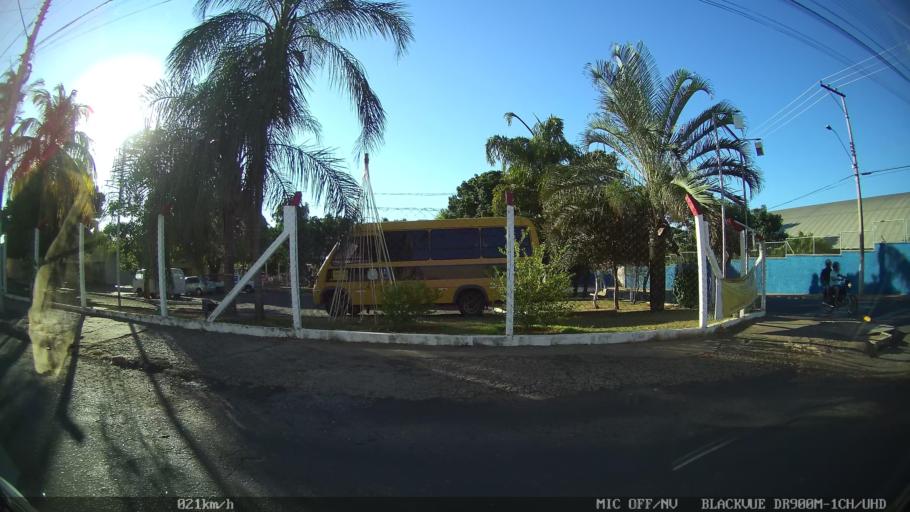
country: BR
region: Sao Paulo
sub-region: Guapiacu
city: Guapiacu
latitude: -20.7945
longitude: -49.2260
